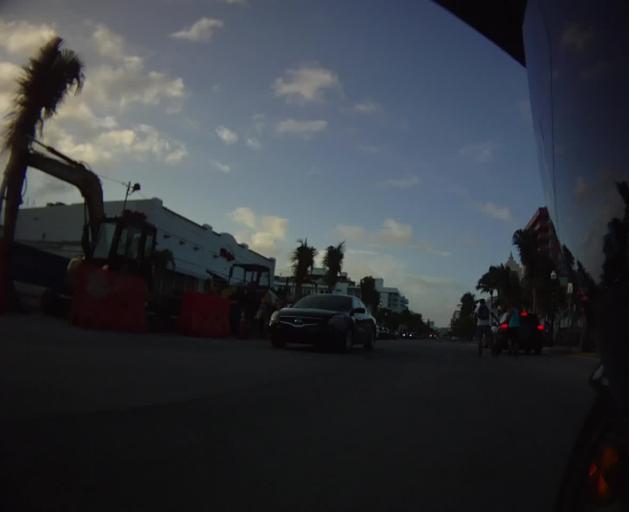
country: US
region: Florida
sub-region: Miami-Dade County
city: Miami Beach
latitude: 25.7688
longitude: -80.1332
